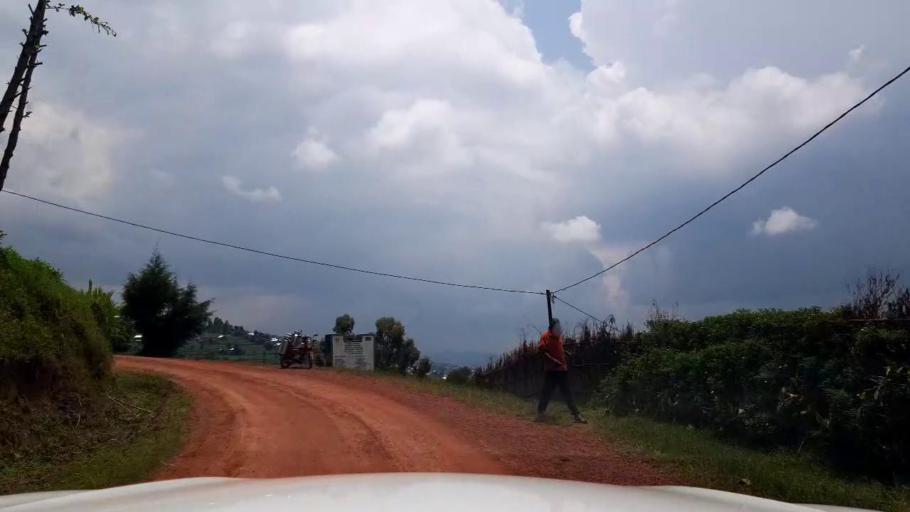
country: RW
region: Northern Province
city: Byumba
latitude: -1.4866
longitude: 29.9247
